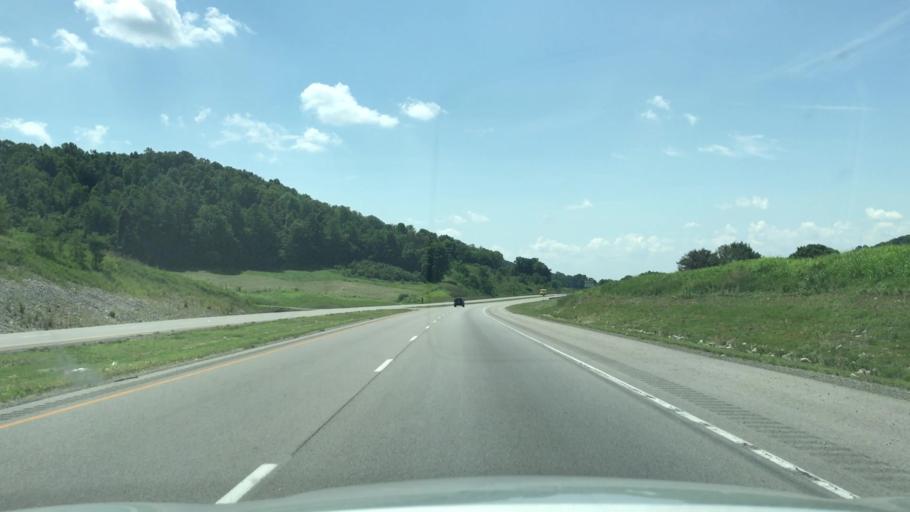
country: US
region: Kentucky
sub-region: Clinton County
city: Albany
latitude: 36.7377
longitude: -85.1341
